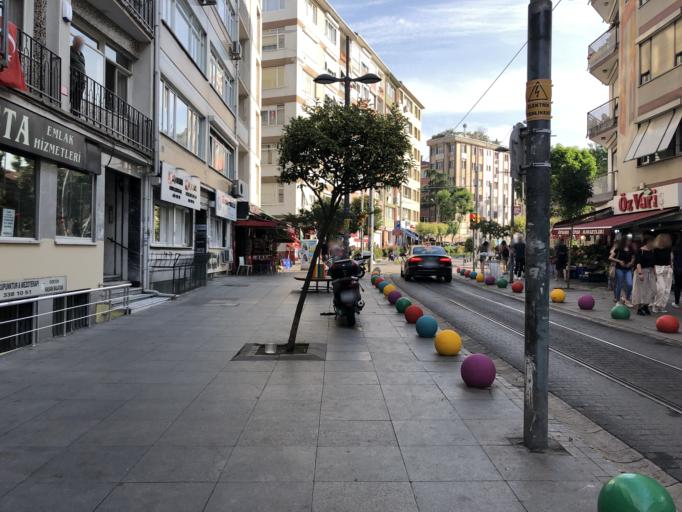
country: TR
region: Istanbul
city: UEskuedar
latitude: 40.9848
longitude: 29.0277
